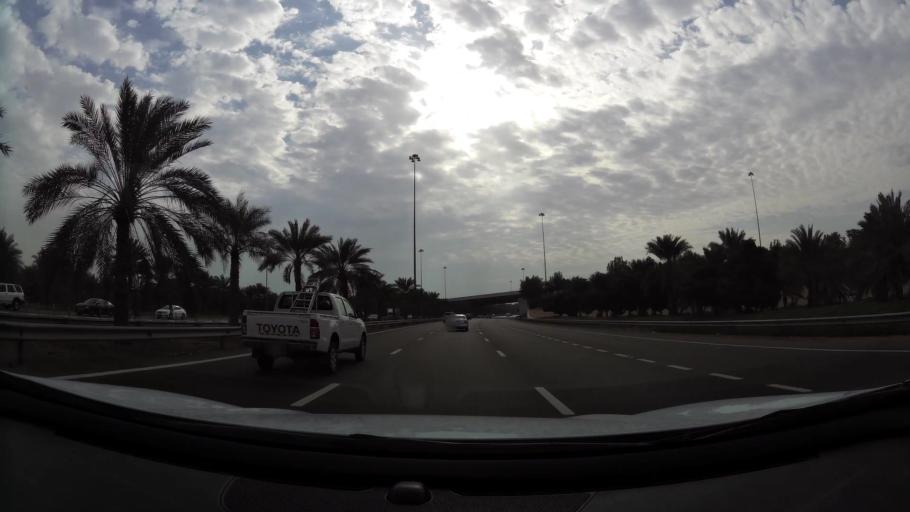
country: AE
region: Abu Dhabi
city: Al Ain
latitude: 24.2008
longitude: 55.5827
